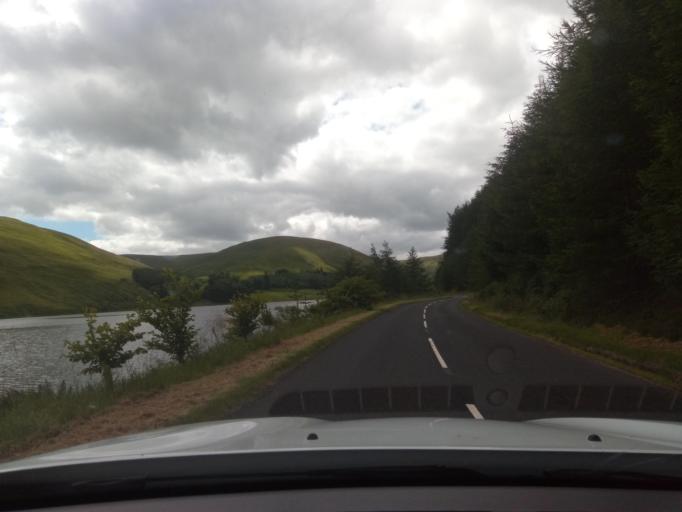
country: GB
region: Scotland
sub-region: The Scottish Borders
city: Peebles
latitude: 55.4668
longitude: -3.2098
